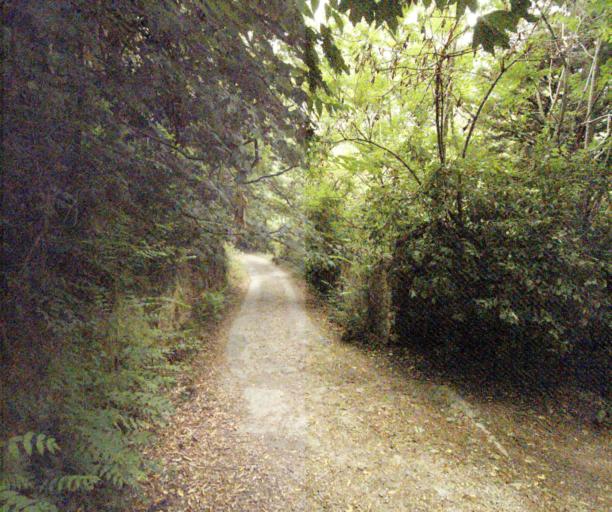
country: FR
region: Midi-Pyrenees
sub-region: Departement du Tarn
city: Soreze
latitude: 43.4423
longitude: 2.0638
